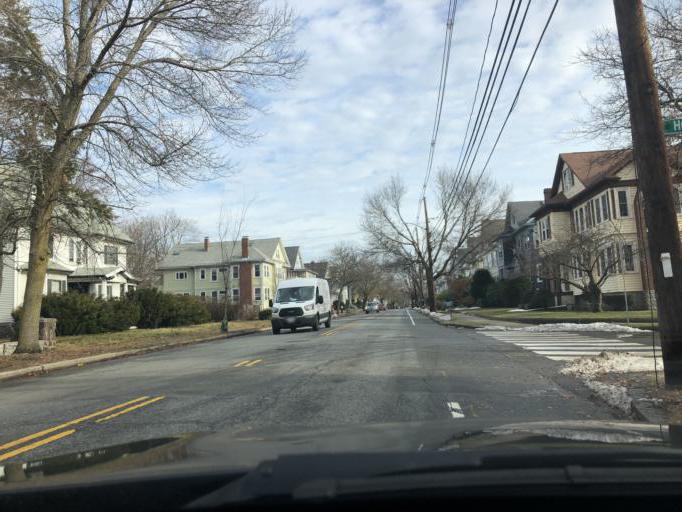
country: US
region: Massachusetts
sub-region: Middlesex County
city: Arlington
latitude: 42.4037
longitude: -71.1507
